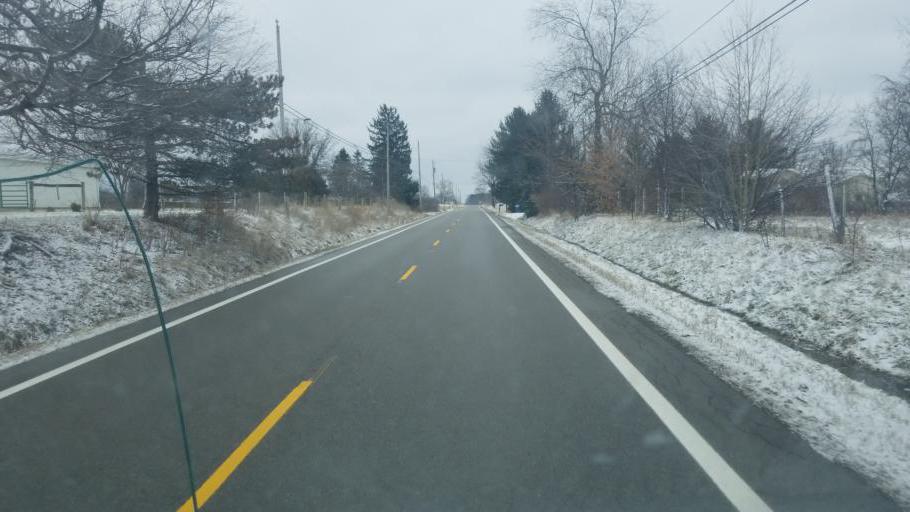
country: US
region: Ohio
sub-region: Licking County
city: Johnstown
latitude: 40.1762
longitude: -82.7297
